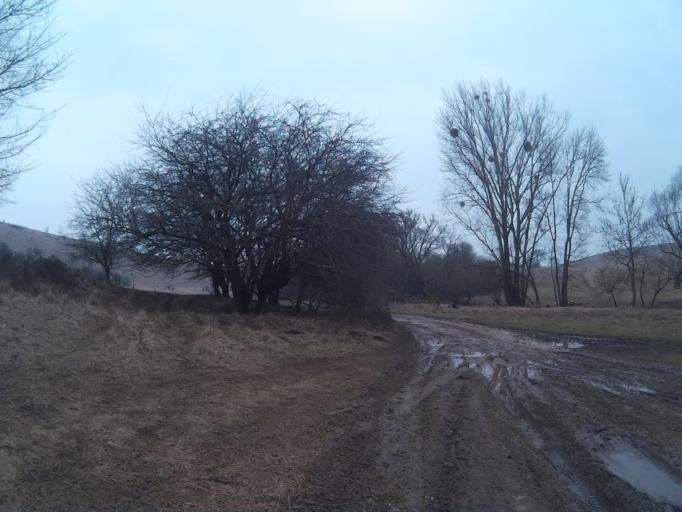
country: HU
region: Fejer
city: Many
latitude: 47.5414
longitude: 18.5815
